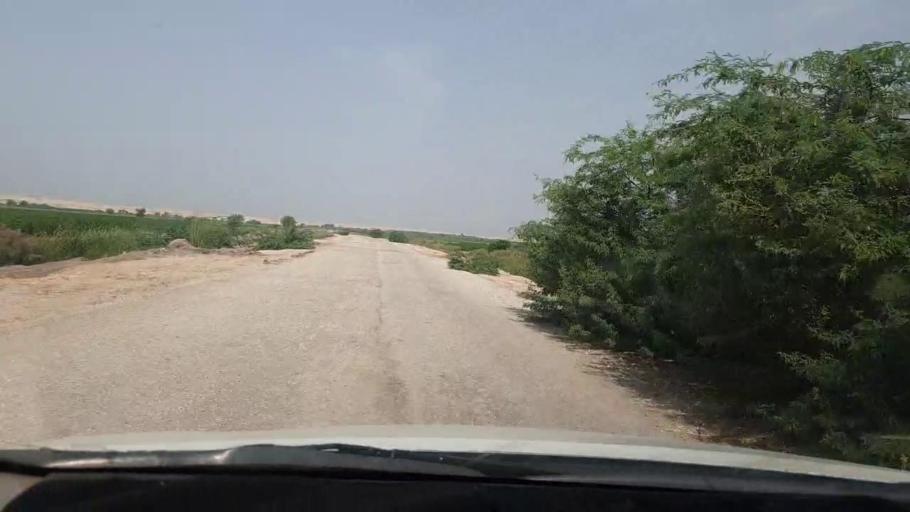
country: PK
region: Sindh
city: Rohri
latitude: 27.5945
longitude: 69.0027
